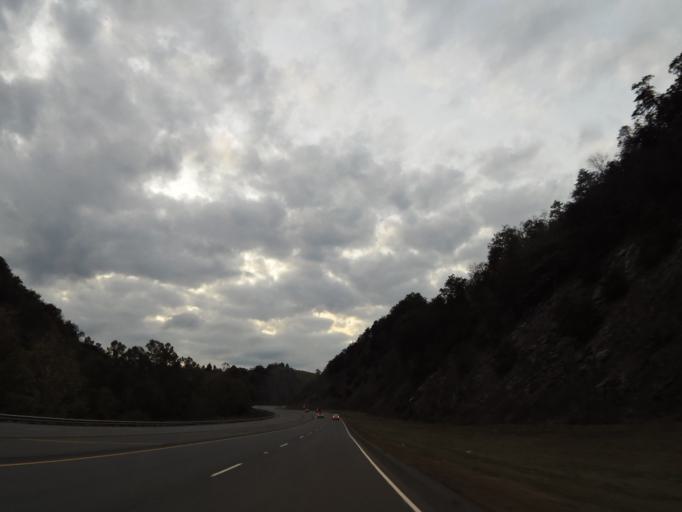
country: US
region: North Carolina
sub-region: Madison County
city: Marshall
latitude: 35.7716
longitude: -82.6251
